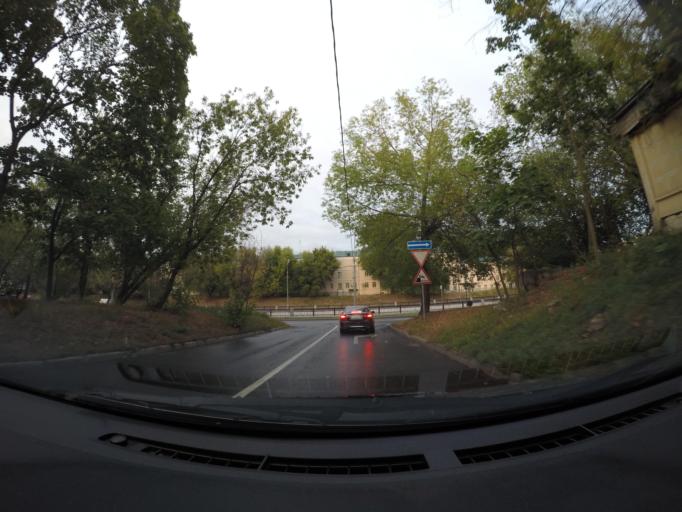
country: RU
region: Moskovskaya
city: Bogorodskoye
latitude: 55.7982
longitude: 37.6990
